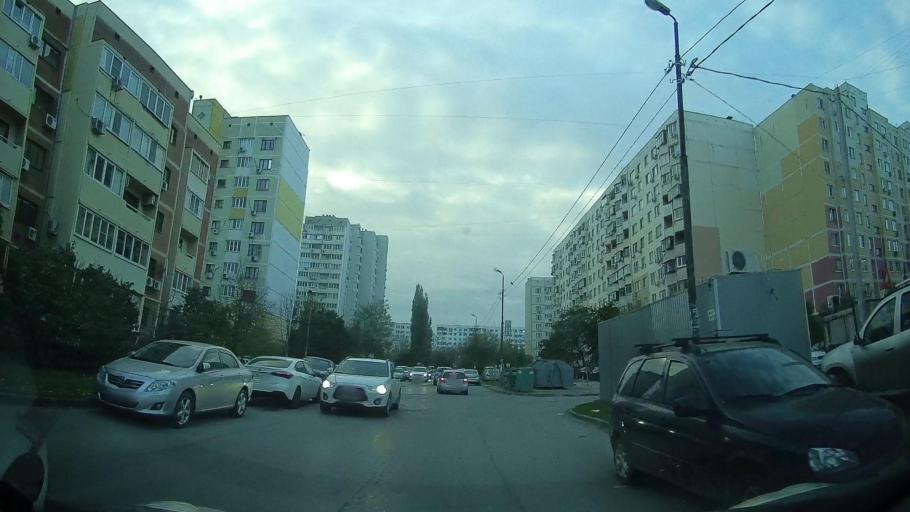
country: RU
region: Rostov
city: Severnyy
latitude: 47.2595
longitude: 39.6435
